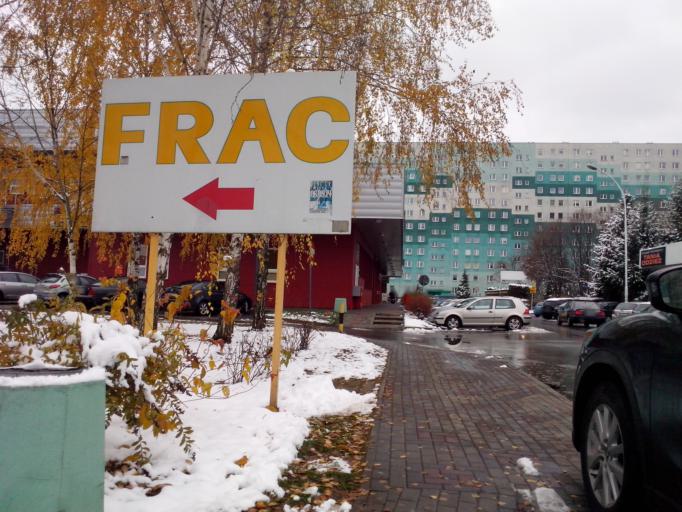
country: PL
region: Subcarpathian Voivodeship
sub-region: Rzeszow
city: Rzeszow
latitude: 50.0216
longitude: 22.0121
